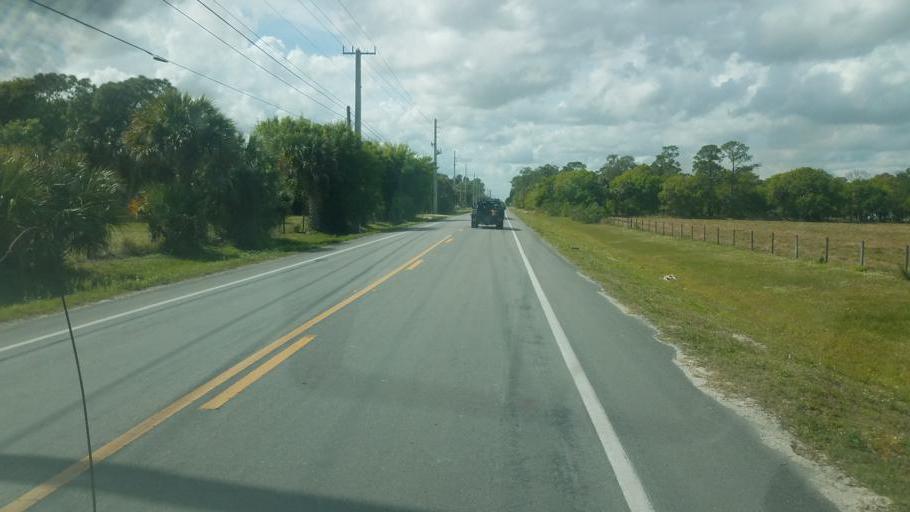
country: US
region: Florida
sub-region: Saint Lucie County
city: Lakewood Park
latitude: 27.4476
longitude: -80.4567
